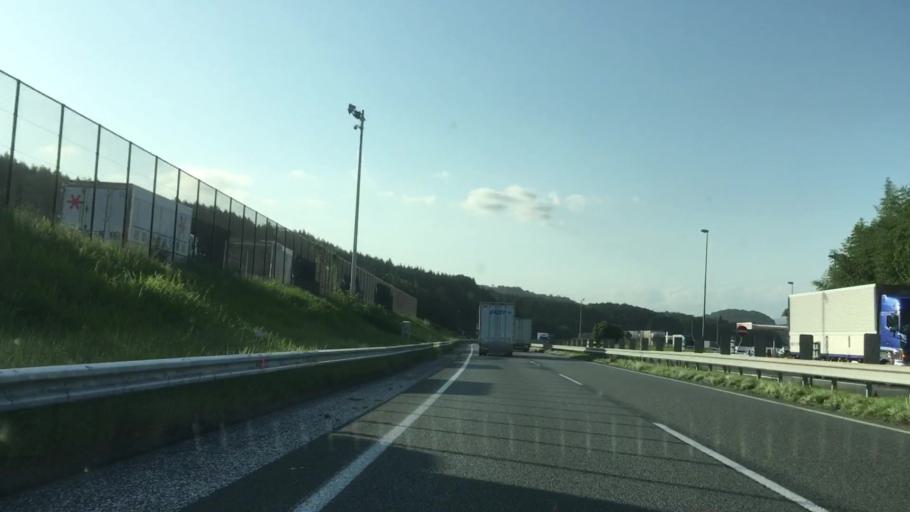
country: JP
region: Yamaguchi
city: Ogori-shimogo
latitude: 34.1530
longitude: 131.3388
